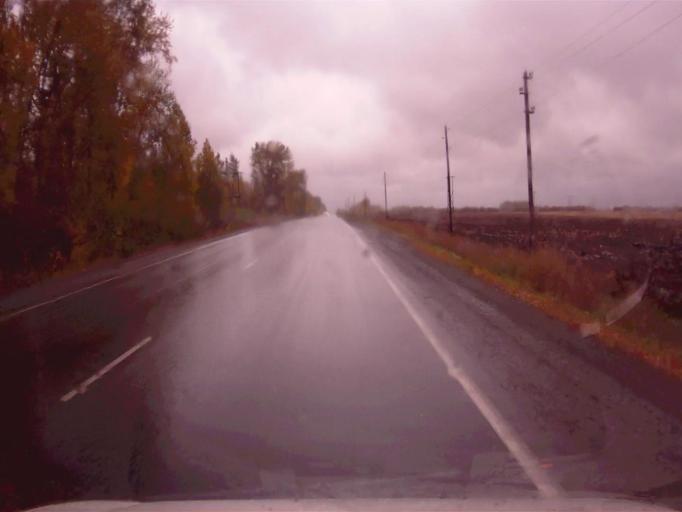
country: RU
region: Chelyabinsk
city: Argayash
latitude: 55.4305
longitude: 60.9905
